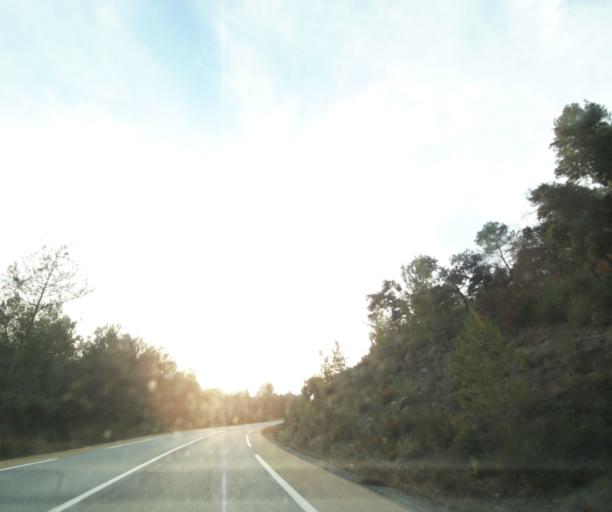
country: FR
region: Provence-Alpes-Cote d'Azur
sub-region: Departement du Var
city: La Motte
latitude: 43.5194
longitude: 6.5242
